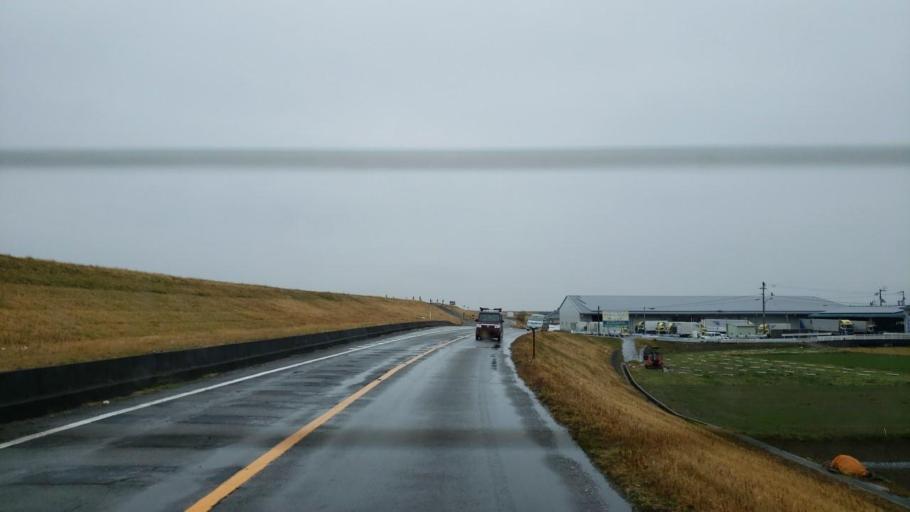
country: JP
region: Tokushima
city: Ishii
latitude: 34.0979
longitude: 134.4097
